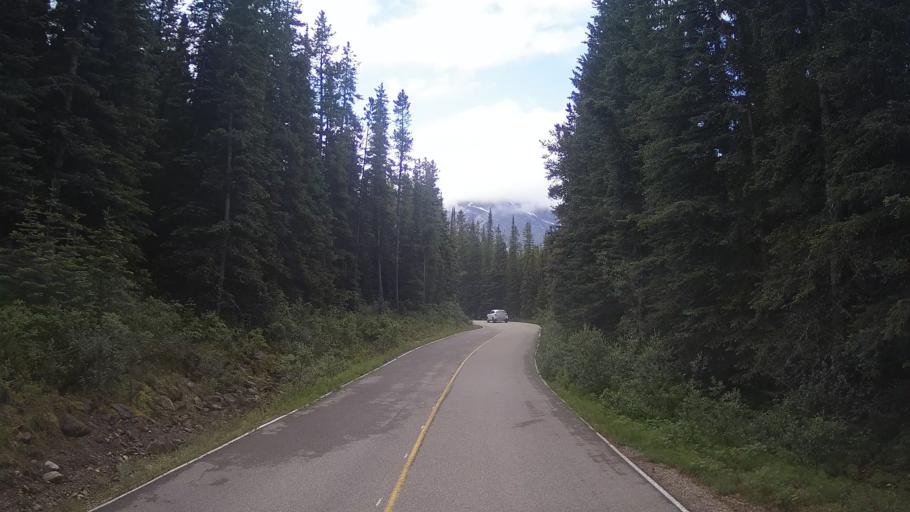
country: CA
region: Alberta
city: Jasper Park Lodge
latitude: 52.7259
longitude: -118.0497
